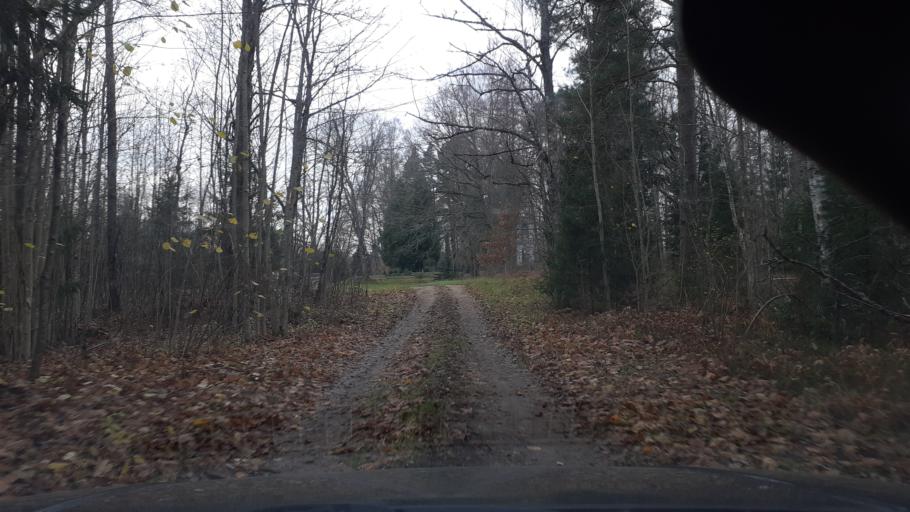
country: LV
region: Alsunga
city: Alsunga
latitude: 56.9423
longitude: 21.6460
